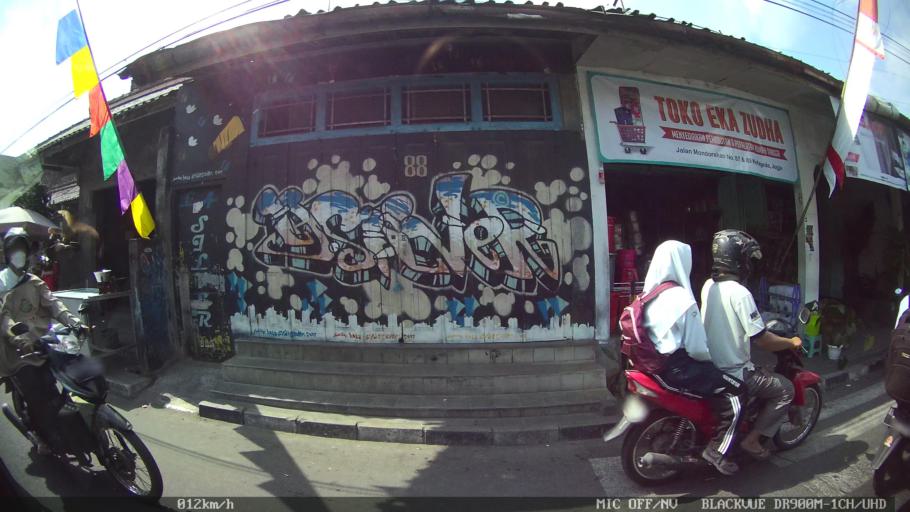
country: ID
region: Daerah Istimewa Yogyakarta
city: Yogyakarta
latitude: -7.8278
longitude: 110.3996
